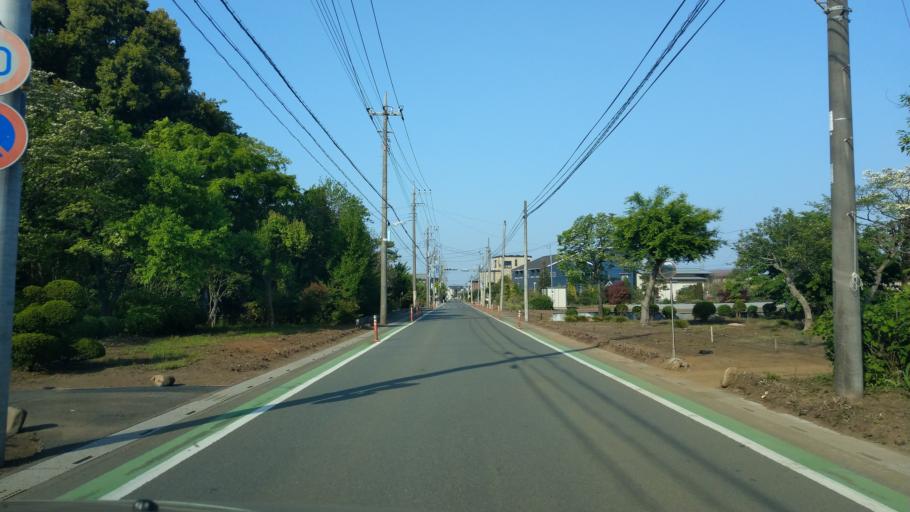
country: JP
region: Saitama
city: Tokorozawa
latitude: 35.8318
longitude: 139.4801
